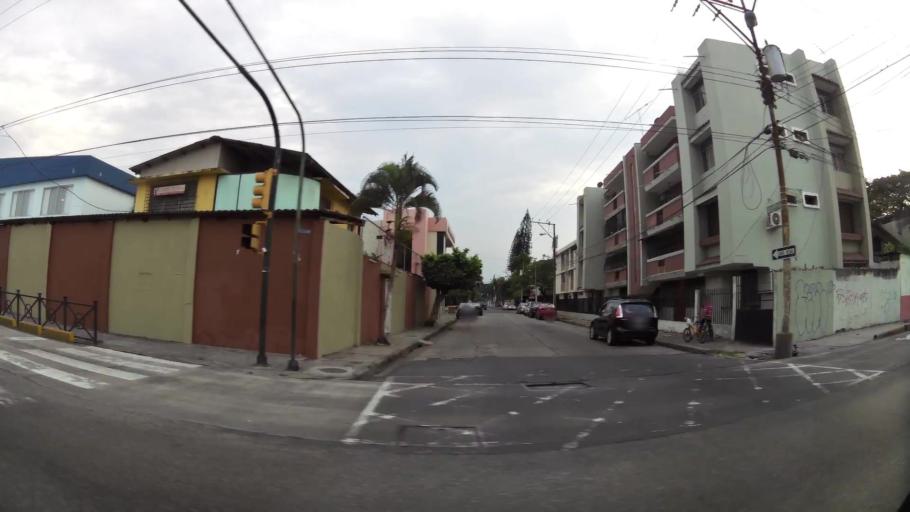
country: EC
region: Guayas
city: Guayaquil
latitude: -2.2248
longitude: -79.8896
